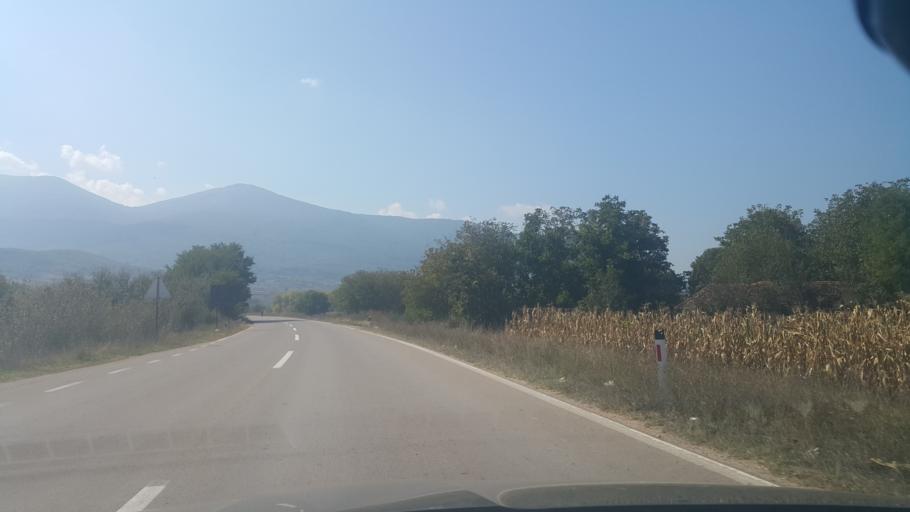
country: RS
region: Central Serbia
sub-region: Pirotski Okrug
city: Bela Palanka
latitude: 43.2306
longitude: 22.3146
